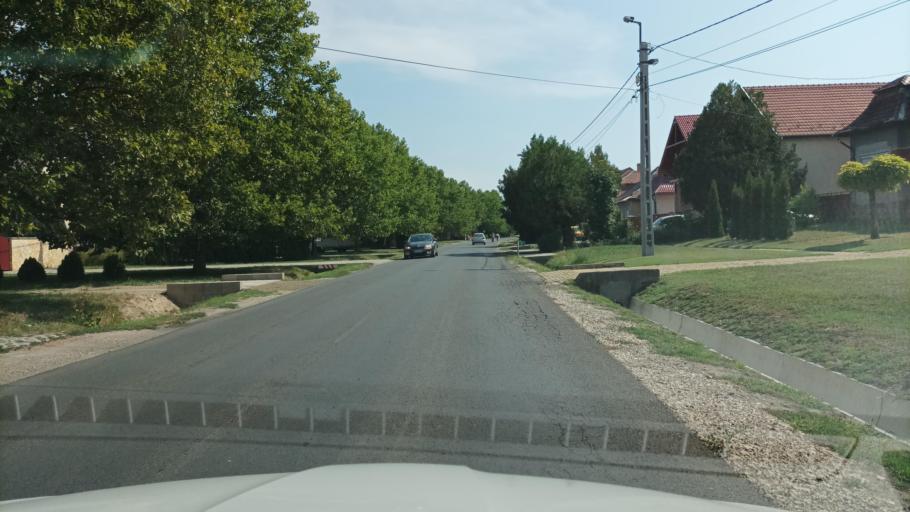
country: HU
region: Pest
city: Galgaheviz
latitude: 47.6220
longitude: 19.5567
